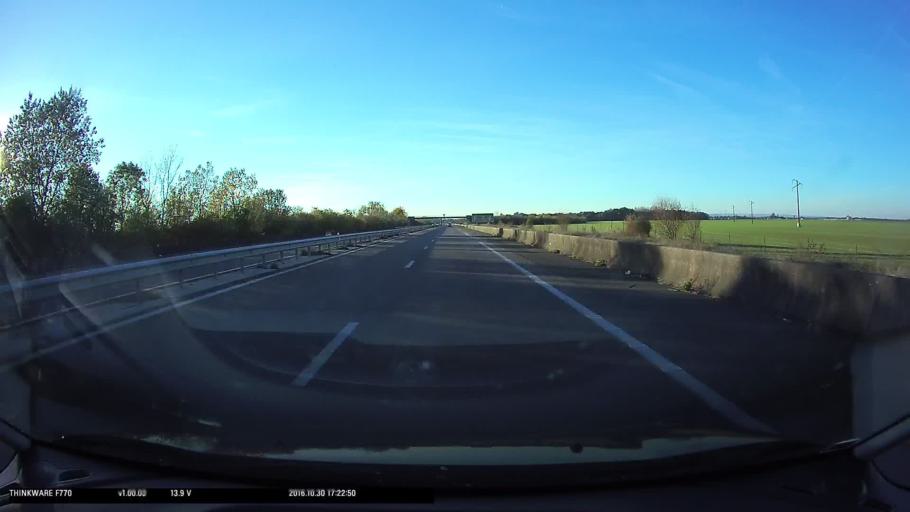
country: FR
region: Bourgogne
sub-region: Departement de la Cote-d'Or
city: Genlis
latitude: 47.2608
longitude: 5.2126
